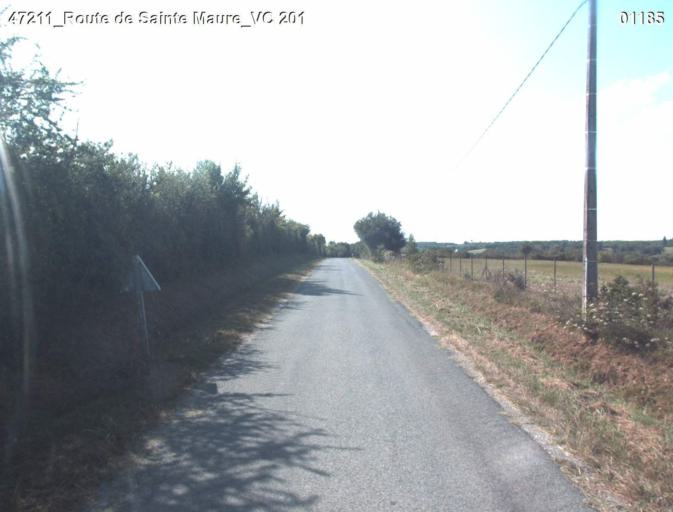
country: FR
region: Aquitaine
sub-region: Departement du Lot-et-Garonne
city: Mezin
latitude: 44.0312
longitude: 0.1907
